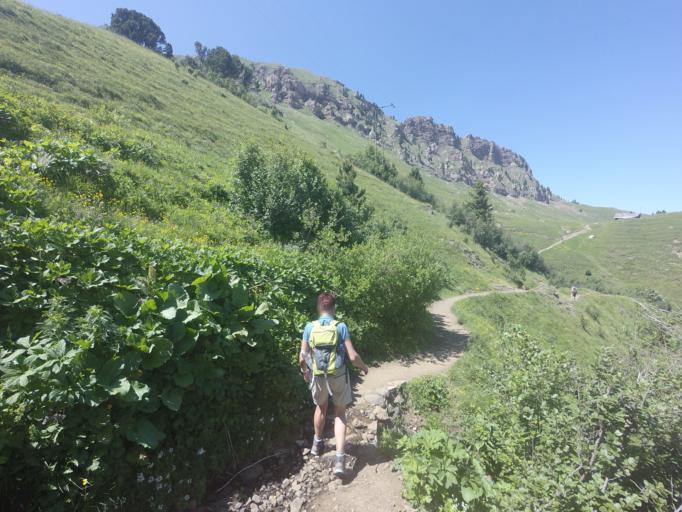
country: IT
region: Trentino-Alto Adige
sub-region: Provincia di Trento
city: Mazzin
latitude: 46.5040
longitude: 11.6507
